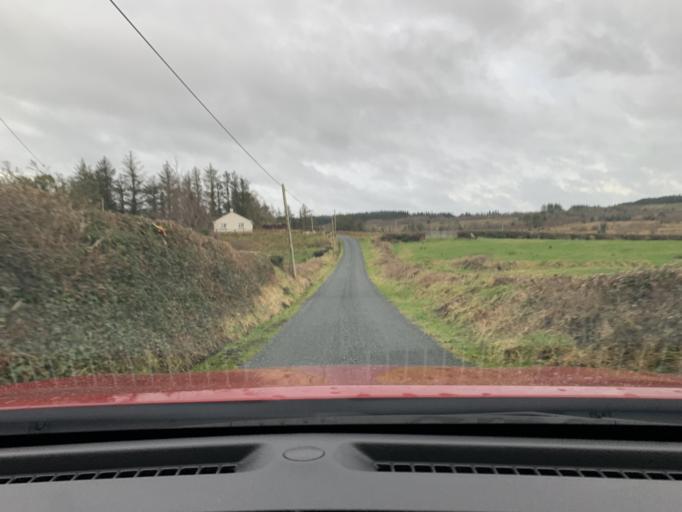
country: IE
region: Connaught
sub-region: Roscommon
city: Ballaghaderreen
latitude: 53.9673
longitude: -8.5164
